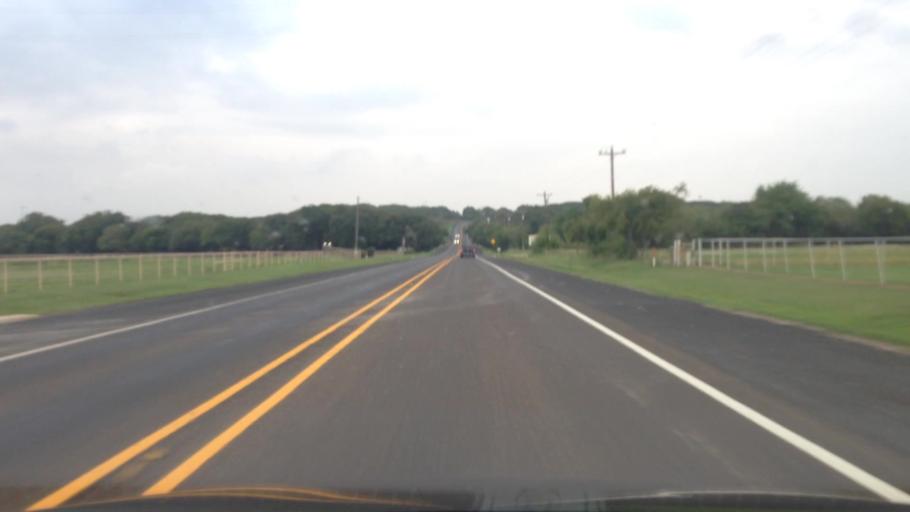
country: US
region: Texas
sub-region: Johnson County
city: Burleson
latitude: 32.5025
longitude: -97.3429
